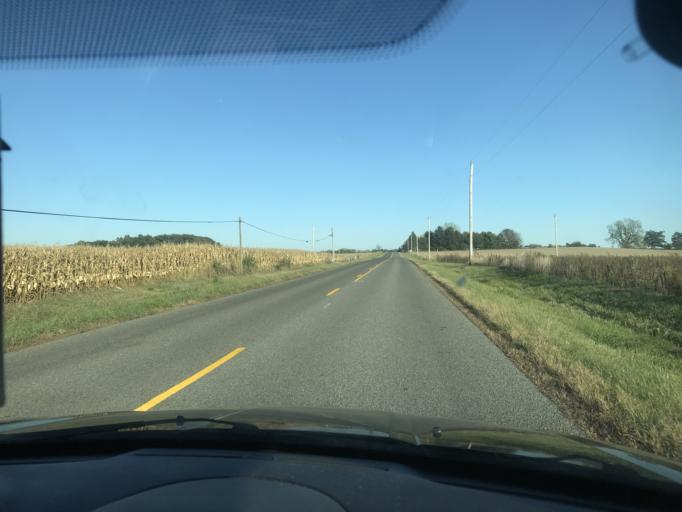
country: US
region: Ohio
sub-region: Logan County
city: Bellefontaine
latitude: 40.3203
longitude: -83.8079
